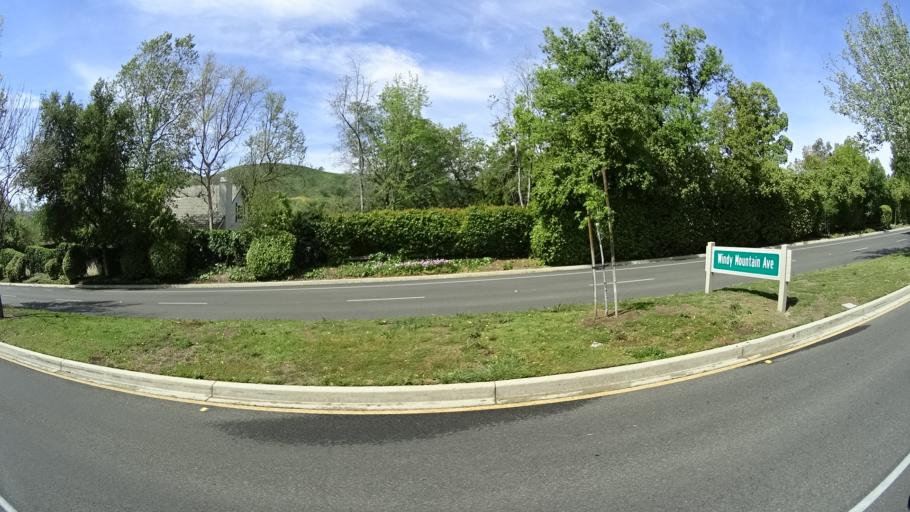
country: US
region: California
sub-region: Ventura County
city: Oak Park
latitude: 34.1897
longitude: -118.7910
